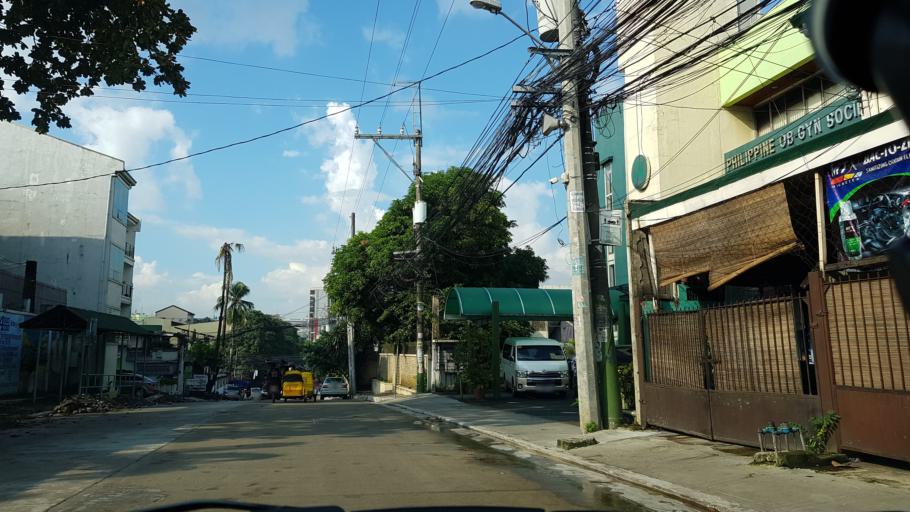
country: PH
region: Metro Manila
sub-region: Quezon City
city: Quezon City
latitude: 14.6365
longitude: 121.0478
